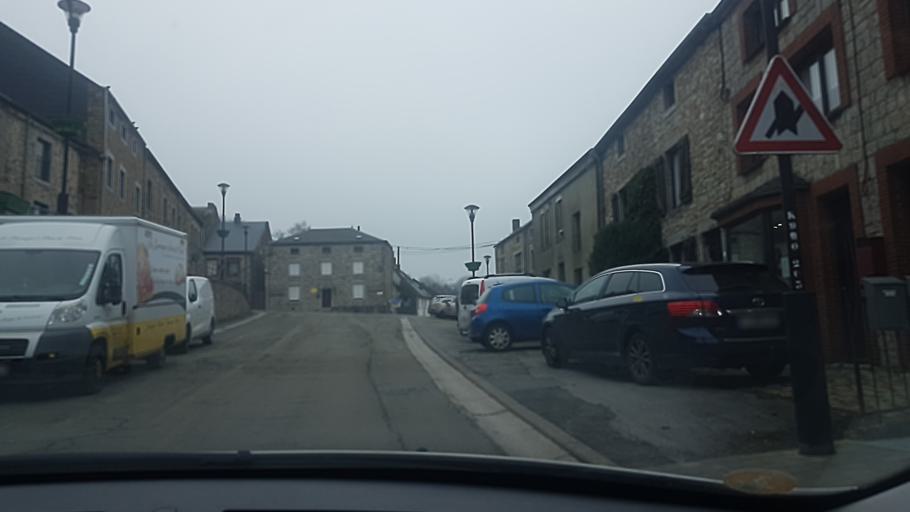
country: FR
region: Champagne-Ardenne
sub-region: Departement des Ardennes
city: Haybes
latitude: 50.0242
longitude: 4.6390
